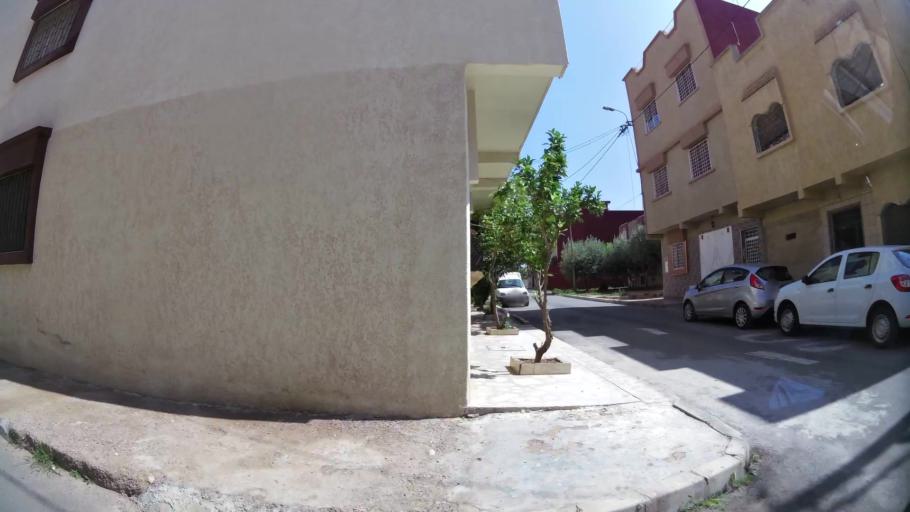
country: MA
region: Oriental
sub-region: Oujda-Angad
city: Oujda
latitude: 34.6909
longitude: -1.8691
